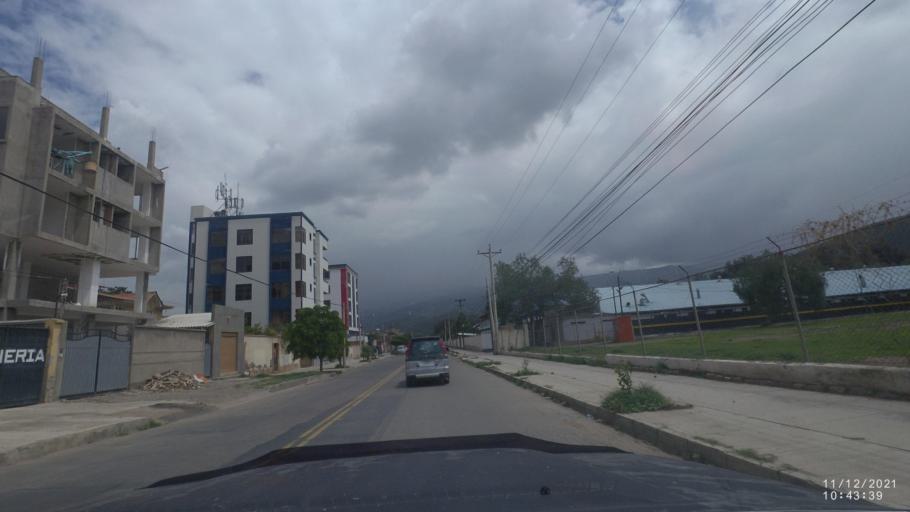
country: BO
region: Cochabamba
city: Cochabamba
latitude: -17.4216
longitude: -66.1311
